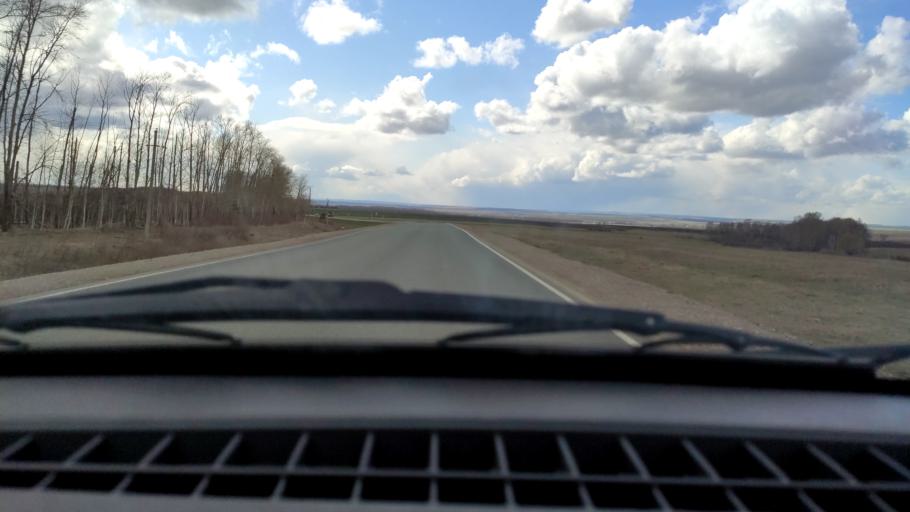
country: RU
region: Bashkortostan
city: Kushnarenkovo
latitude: 55.0579
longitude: 55.1715
